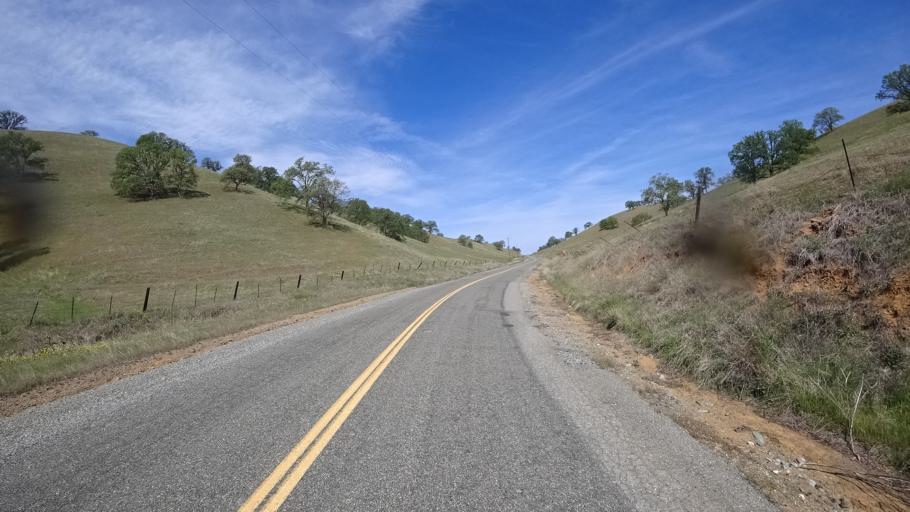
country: US
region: California
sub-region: Glenn County
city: Willows
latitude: 39.5684
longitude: -122.4425
